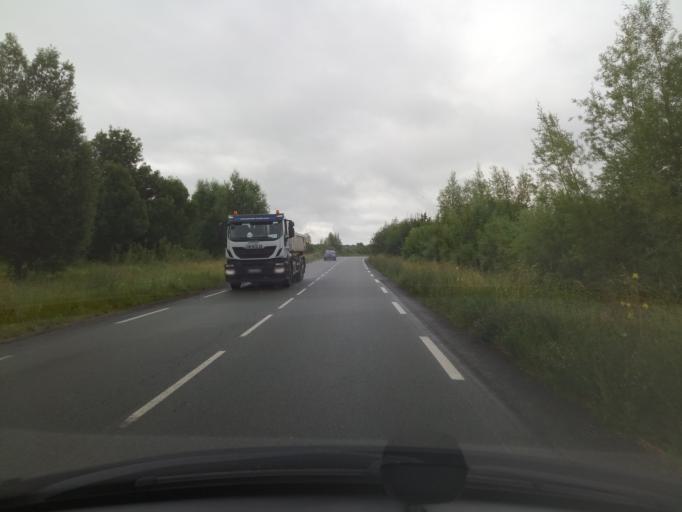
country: FR
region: Poitou-Charentes
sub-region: Departement de la Charente-Maritime
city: Courcon
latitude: 46.1909
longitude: -0.8581
